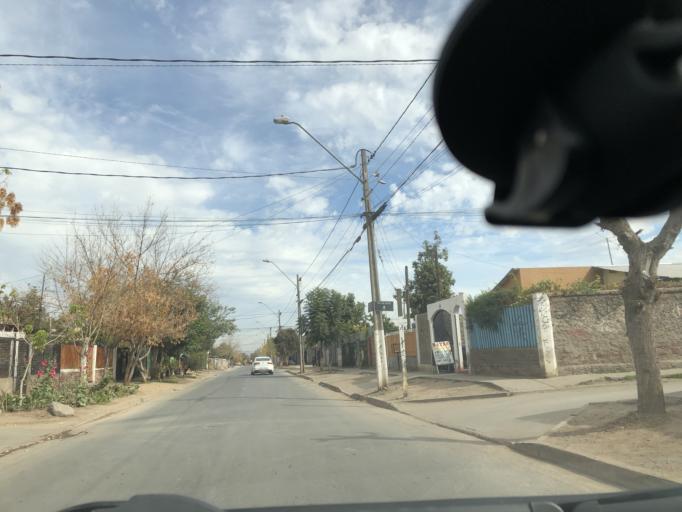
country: CL
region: Santiago Metropolitan
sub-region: Provincia de Cordillera
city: Puente Alto
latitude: -33.6095
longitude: -70.5181
